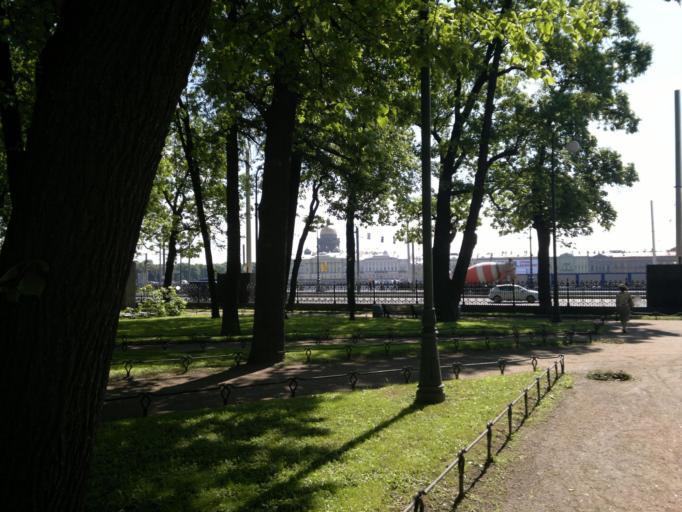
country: RU
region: St.-Petersburg
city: Saint Petersburg
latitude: 59.9383
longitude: 30.2928
